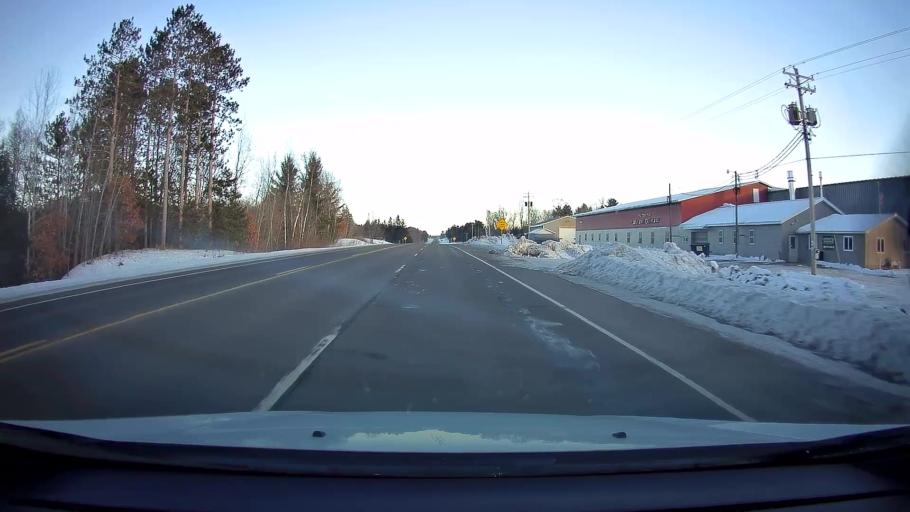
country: US
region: Wisconsin
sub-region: Barron County
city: Cumberland
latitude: 45.5721
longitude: -92.0174
